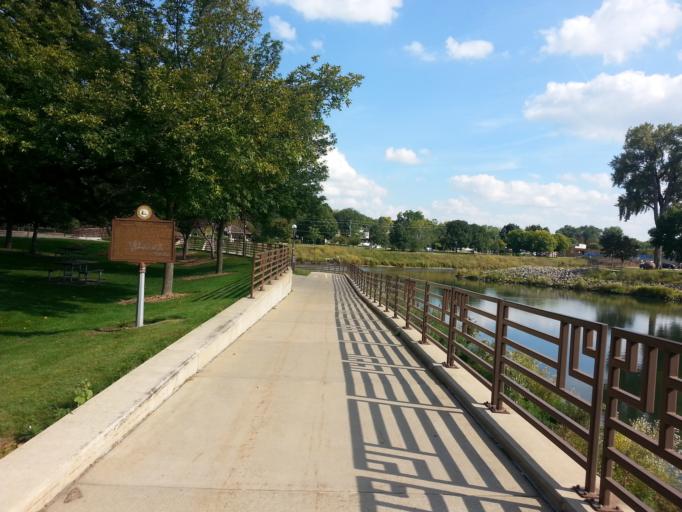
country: US
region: Minnesota
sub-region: Olmsted County
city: Rochester
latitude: 44.0210
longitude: -92.4576
